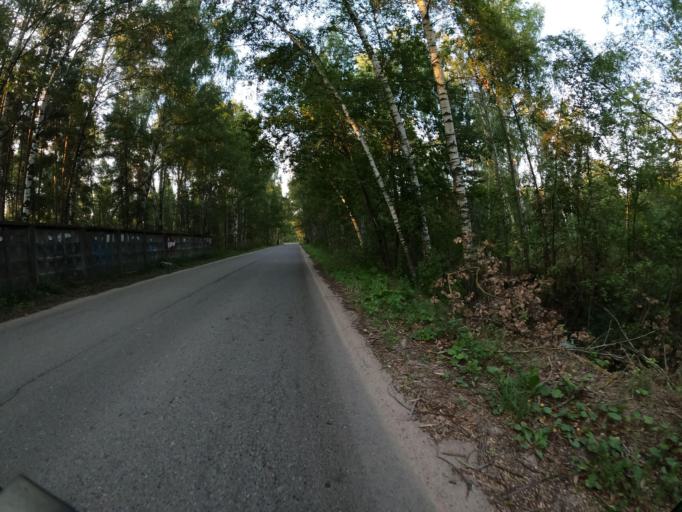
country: RU
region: Moskovskaya
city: Malyshevo
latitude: 55.5205
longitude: 38.2948
